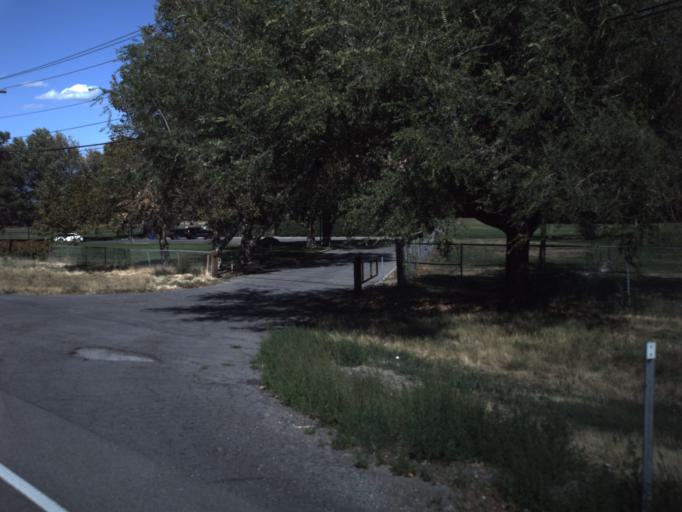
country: US
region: Utah
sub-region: Salt Lake County
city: Salt Lake City
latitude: 40.7945
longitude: -111.9392
